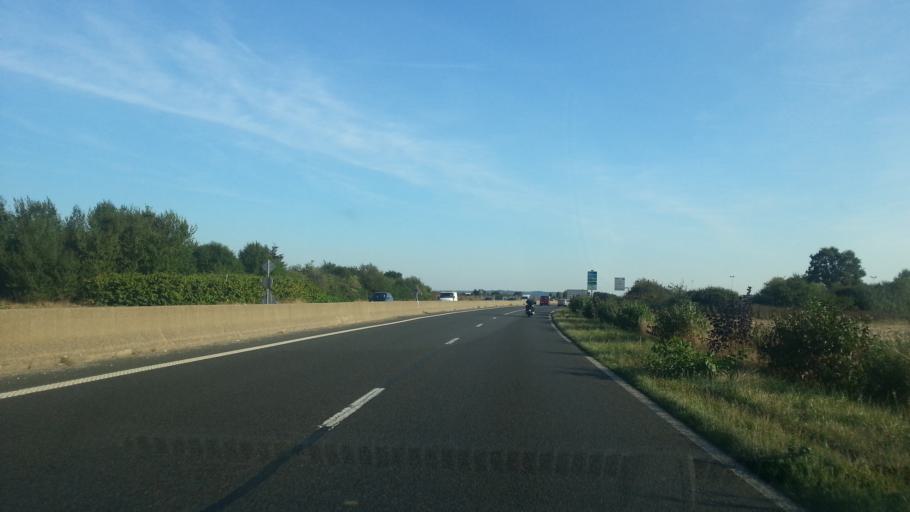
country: FR
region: Picardie
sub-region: Departement de l'Oise
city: Tille
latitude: 49.4435
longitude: 2.1108
